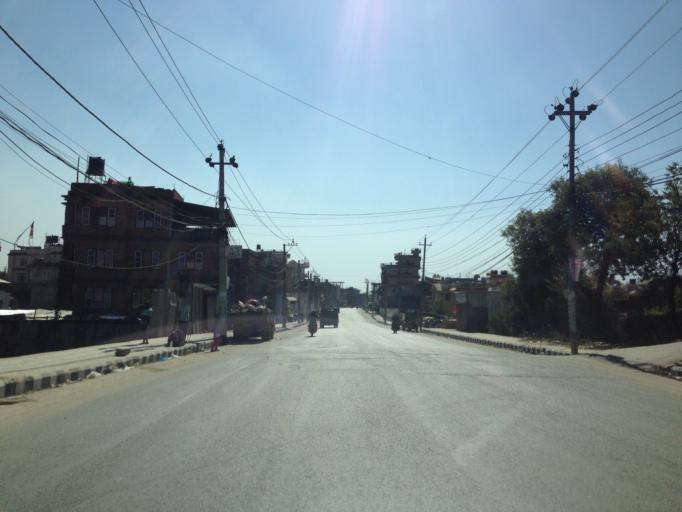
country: NP
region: Central Region
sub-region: Bagmati Zone
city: Kathmandu
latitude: 27.7625
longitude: 85.3527
